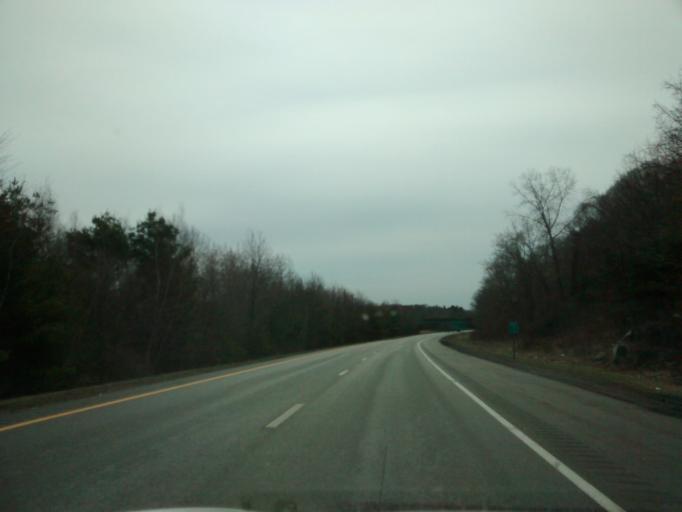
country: US
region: Massachusetts
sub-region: Worcester County
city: Auburn
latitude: 42.1720
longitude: -71.8442
